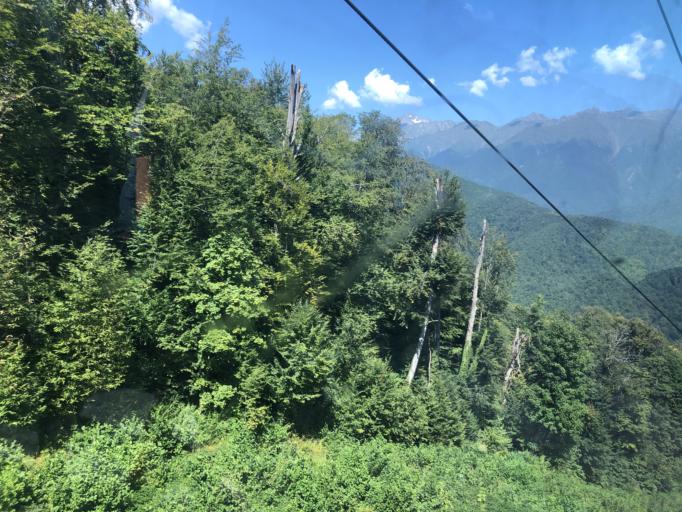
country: RU
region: Krasnodarskiy
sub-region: Sochi City
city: Krasnaya Polyana
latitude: 43.6752
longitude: 40.2625
